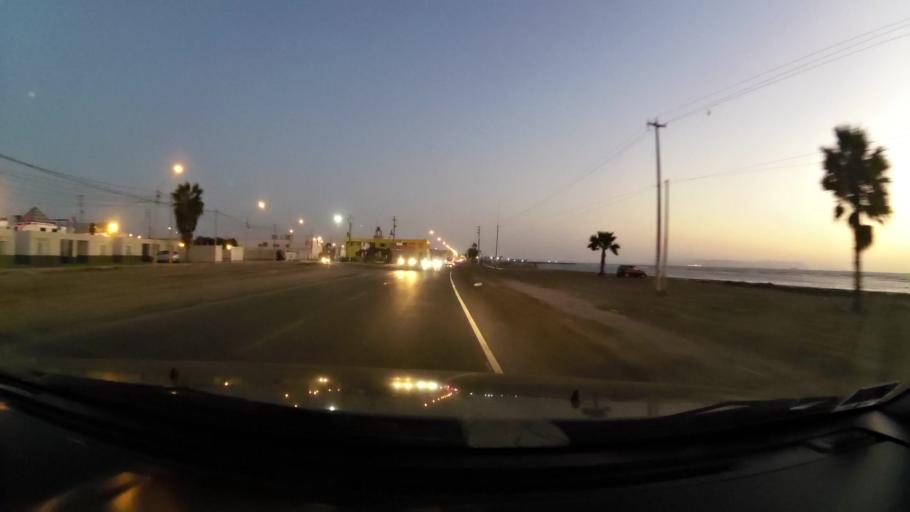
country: PE
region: Ica
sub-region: Provincia de Pisco
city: Pisco
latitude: -13.7264
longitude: -76.2222
